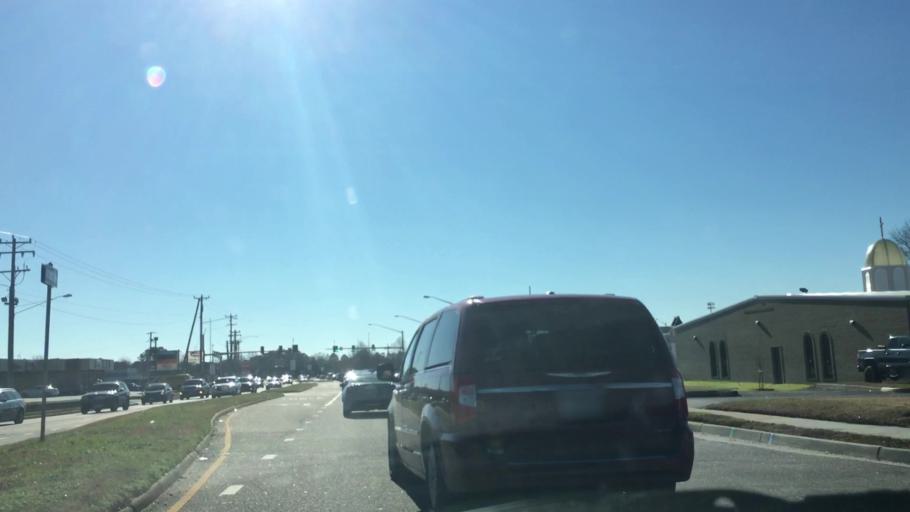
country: US
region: Virginia
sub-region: City of Virginia Beach
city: Virginia Beach
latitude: 36.8501
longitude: -76.0223
